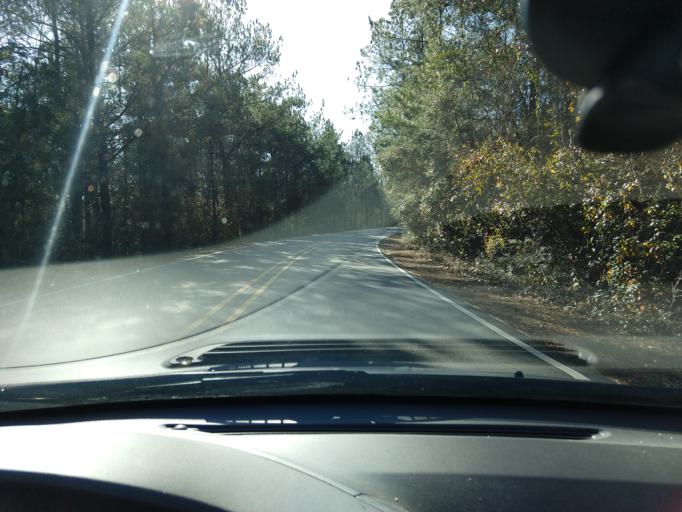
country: US
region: Mississippi
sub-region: Jackson County
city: Gulf Park Estates
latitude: 30.4043
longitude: -88.7784
